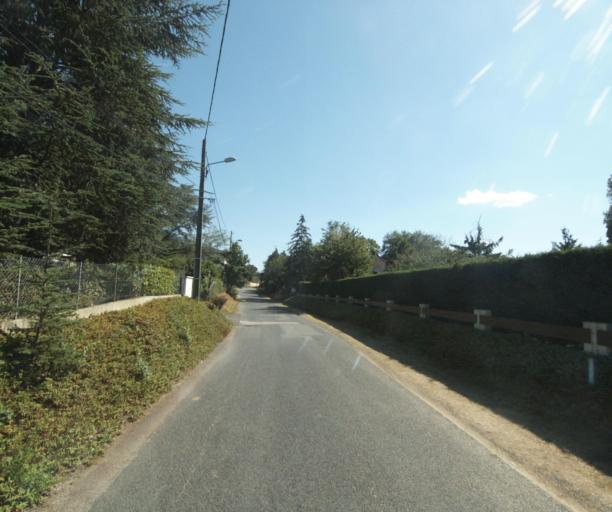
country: FR
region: Rhone-Alpes
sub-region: Departement du Rhone
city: La Tour-de-Salvagny
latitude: 45.8357
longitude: 4.7061
